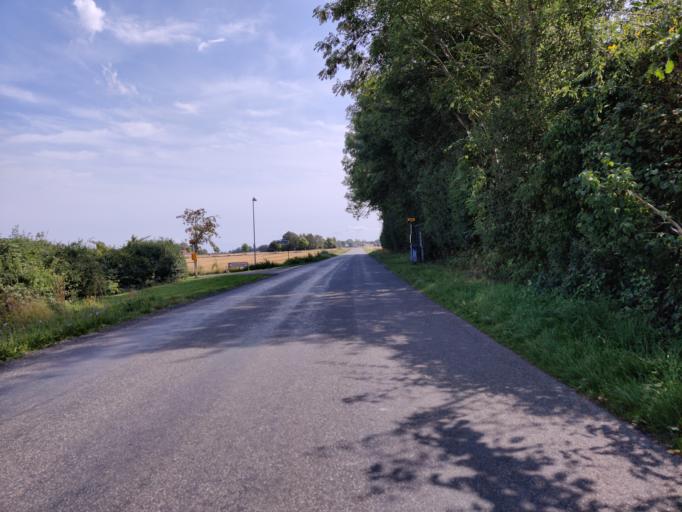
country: DK
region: Zealand
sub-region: Guldborgsund Kommune
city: Nykobing Falster
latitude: 54.6442
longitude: 11.8933
